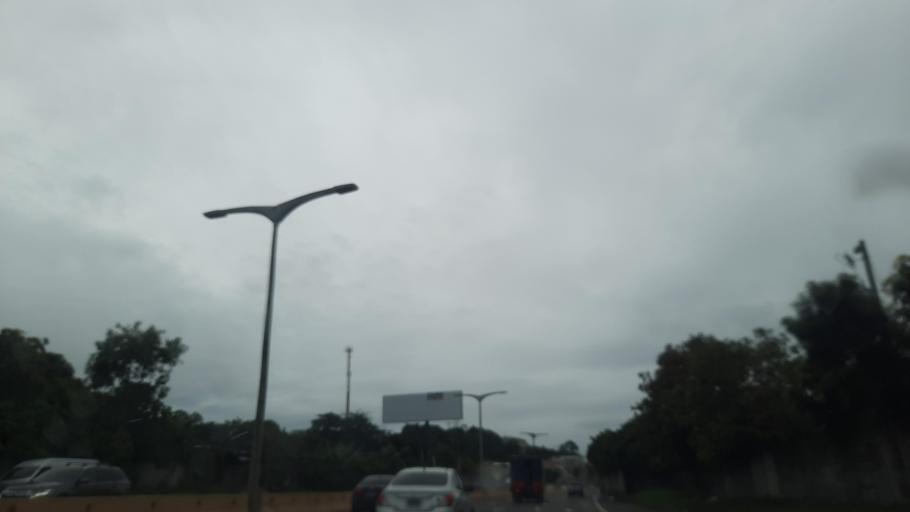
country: SV
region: La Libertad
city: Santa Tecla
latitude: 13.6862
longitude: -89.2928
